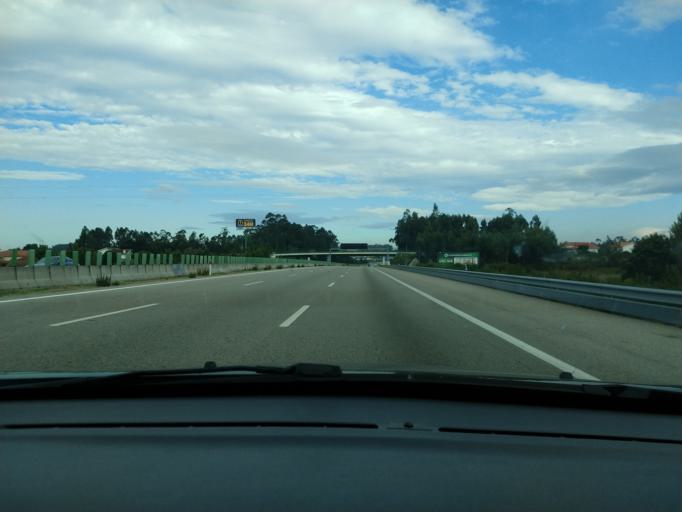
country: PT
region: Aveiro
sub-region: Santa Maria da Feira
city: Feira
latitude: 40.9087
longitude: -8.5672
